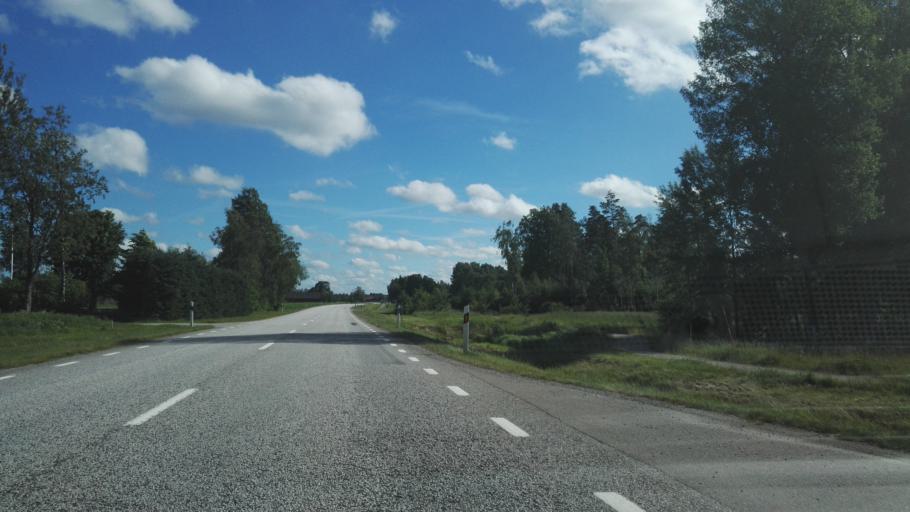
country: SE
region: Joenkoeping
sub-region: Savsjo Kommun
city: Vrigstad
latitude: 57.3418
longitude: 14.4708
